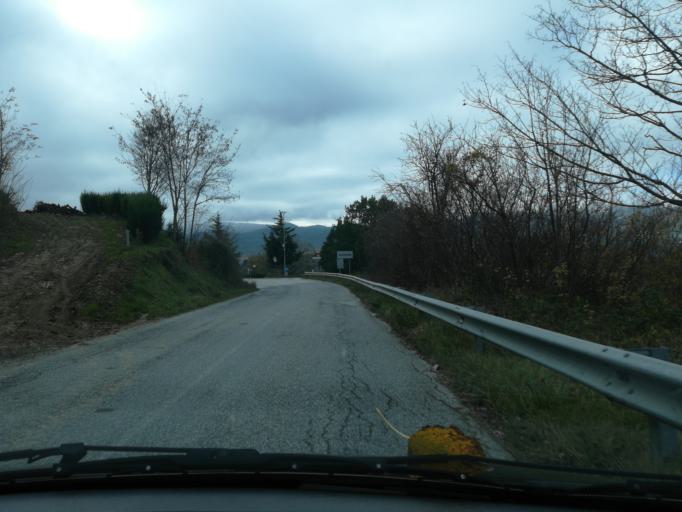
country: IT
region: Molise
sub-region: Provincia di Isernia
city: Agnone
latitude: 41.8180
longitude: 14.3726
